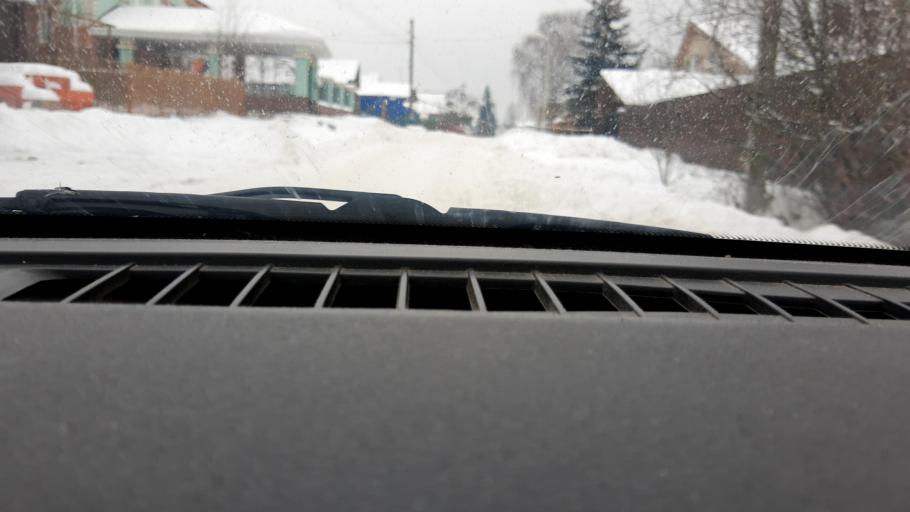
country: RU
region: Nizjnij Novgorod
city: Afonino
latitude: 56.1943
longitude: 44.0619
